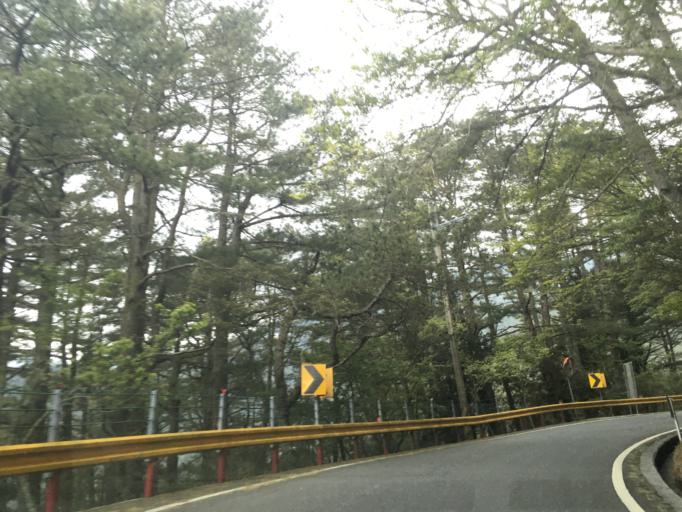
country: TW
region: Taiwan
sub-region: Hualien
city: Hualian
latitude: 24.1795
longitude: 121.3140
